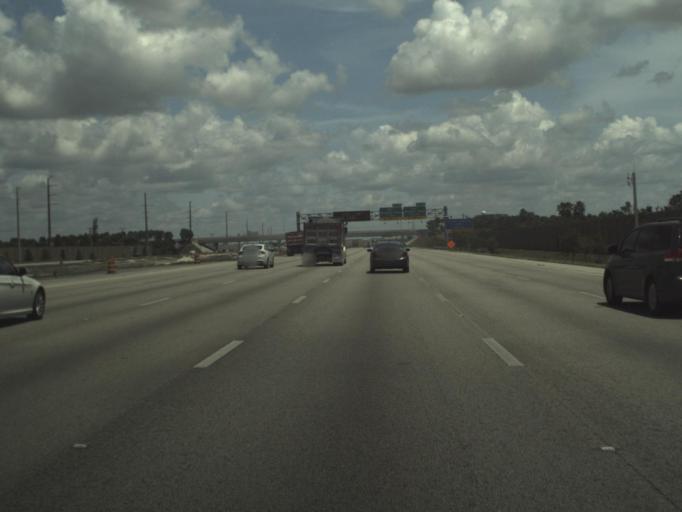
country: US
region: Florida
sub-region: Miami-Dade County
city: Palm Springs North
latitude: 25.9632
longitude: -80.3516
